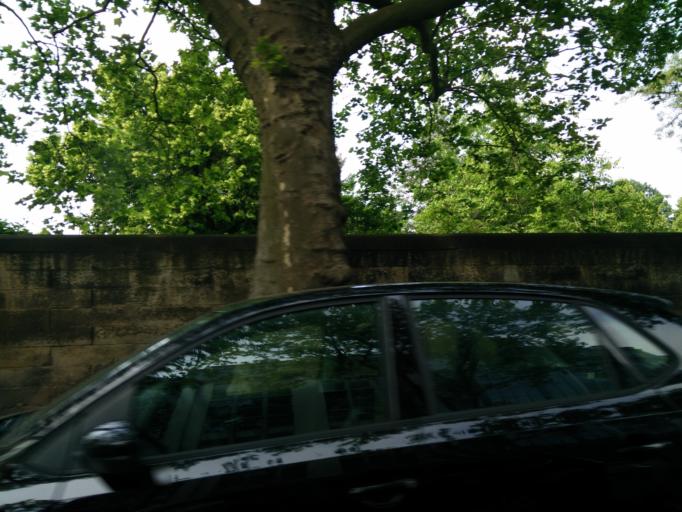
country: DE
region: Saxony
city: Dresden
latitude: 51.0612
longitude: 13.6990
